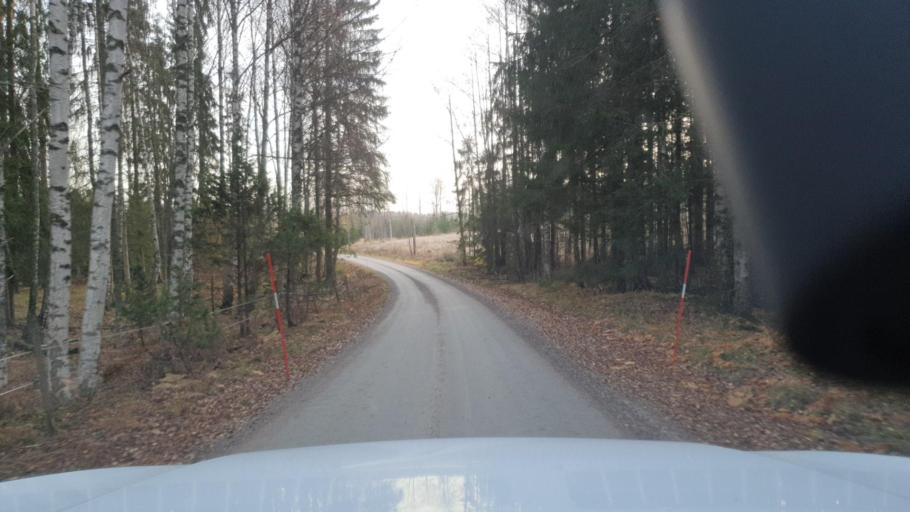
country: SE
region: Uppsala
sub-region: Alvkarleby Kommun
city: AElvkarleby
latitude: 60.4912
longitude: 17.4761
